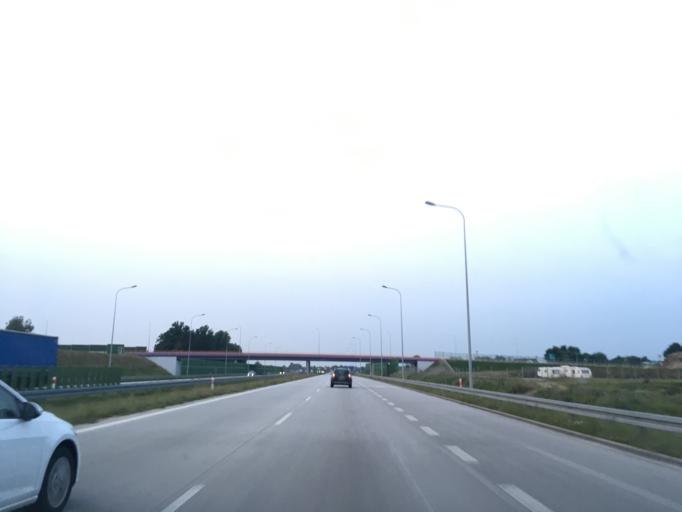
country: PL
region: Lodz Voivodeship
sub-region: Powiat lodzki wschodni
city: Andrespol
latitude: 51.7948
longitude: 19.6185
